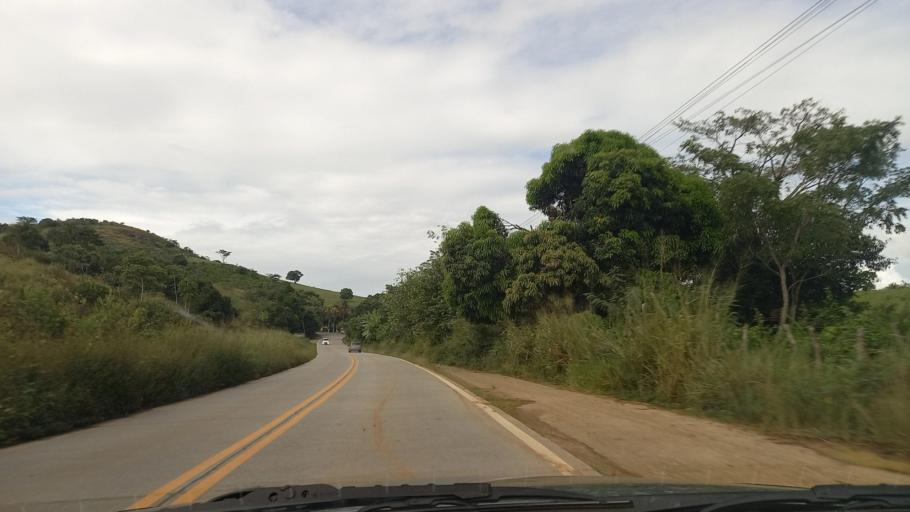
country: BR
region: Pernambuco
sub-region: Catende
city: Catende
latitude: -8.6935
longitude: -35.7253
